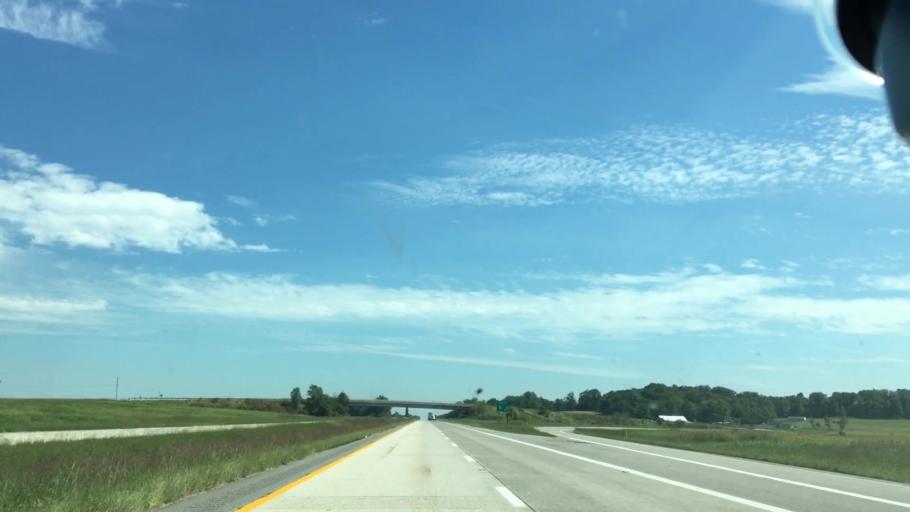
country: US
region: Kentucky
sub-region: Henderson County
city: Henderson
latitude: 37.7873
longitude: -87.4755
